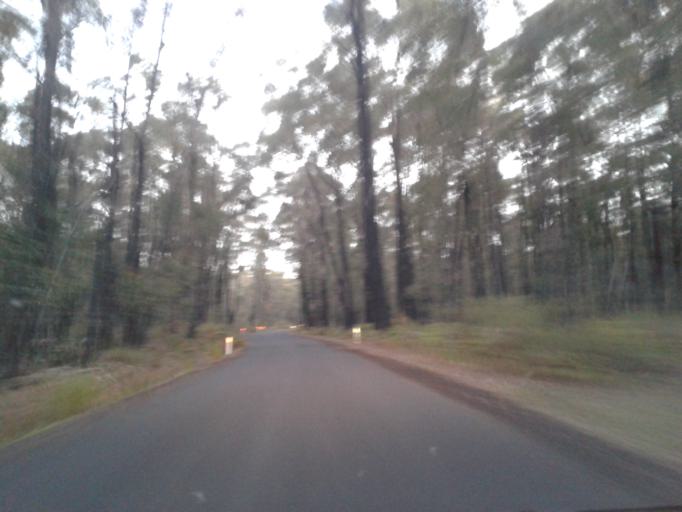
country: AU
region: Victoria
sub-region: Northern Grampians
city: Stawell
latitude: -37.1698
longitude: 142.5039
